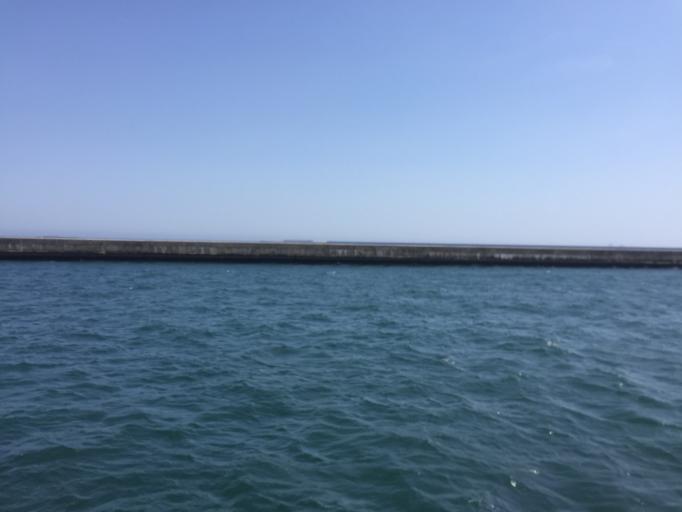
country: JP
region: Fukushima
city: Iwaki
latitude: 36.9202
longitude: 140.8878
